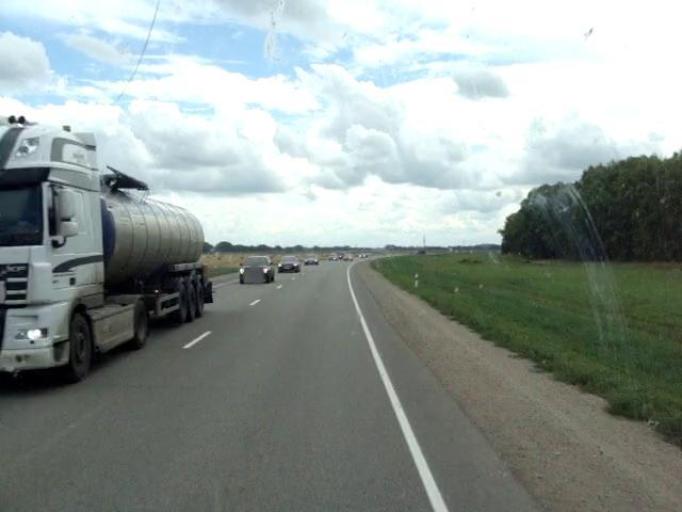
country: RU
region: Altai Krai
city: Shubenka
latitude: 52.6845
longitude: 85.0431
